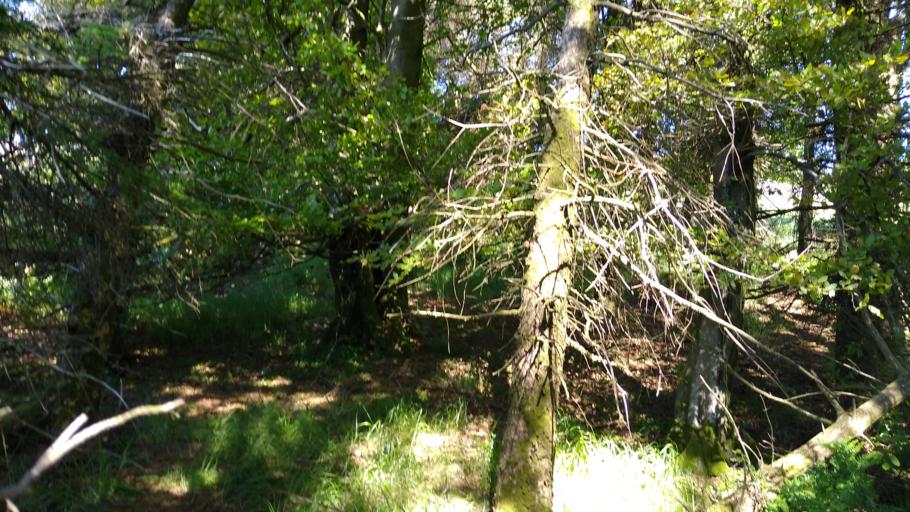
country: GB
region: England
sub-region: Cumbria
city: Wigton
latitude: 54.7525
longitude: -3.0818
